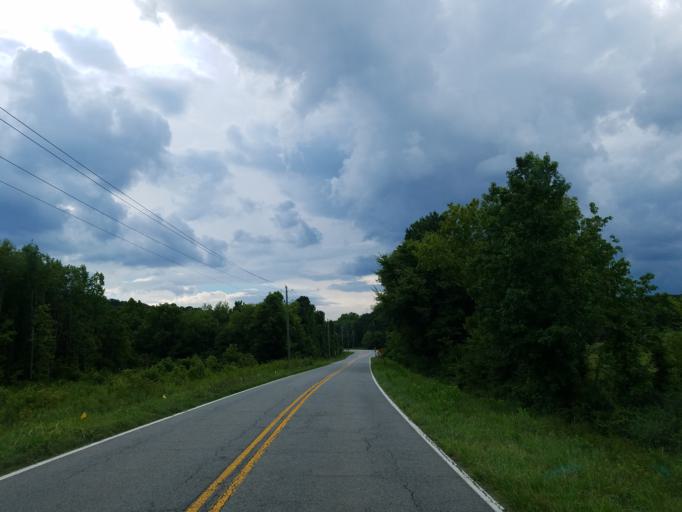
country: US
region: Georgia
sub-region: Bartow County
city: Rydal
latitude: 34.2731
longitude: -84.7610
